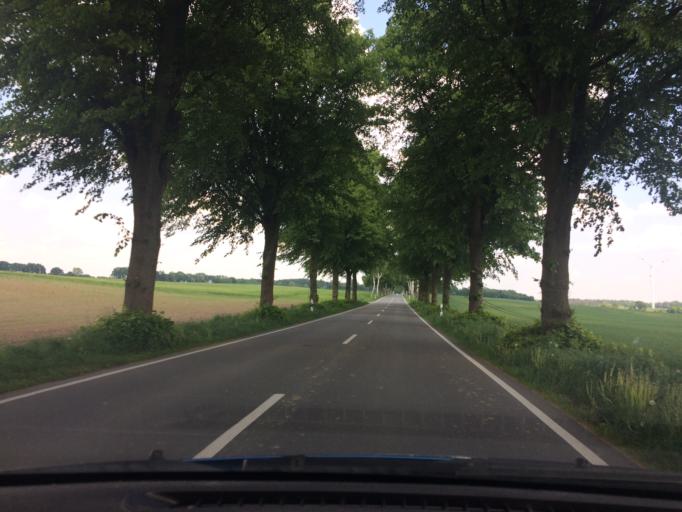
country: DE
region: Lower Saxony
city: Dahlem
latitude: 53.1927
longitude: 10.7793
